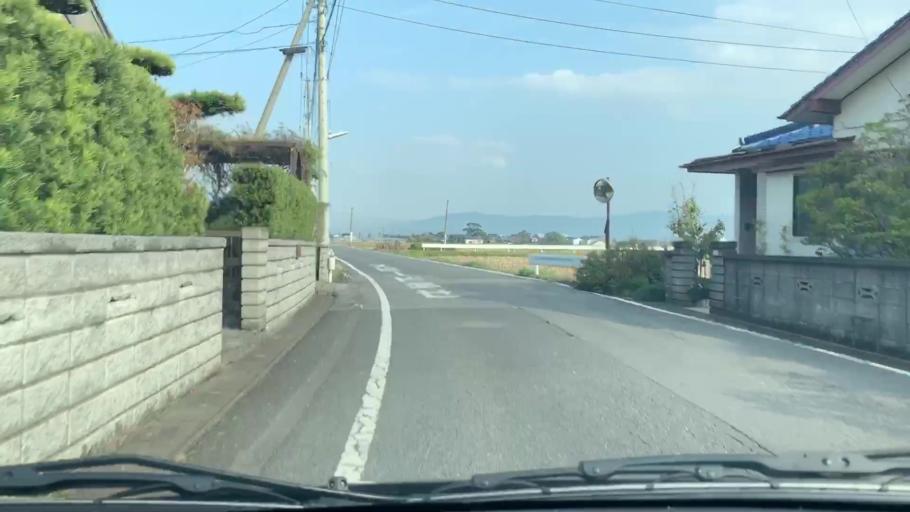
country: JP
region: Saga Prefecture
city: Saga-shi
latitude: 33.2487
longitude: 130.2582
